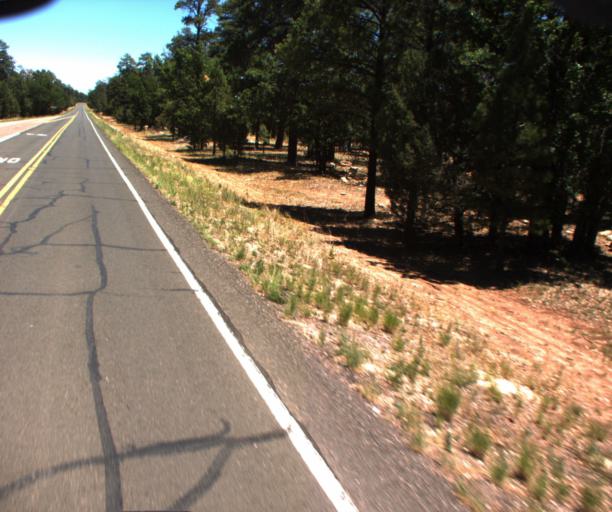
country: US
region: Arizona
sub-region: Gila County
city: Star Valley
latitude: 34.6237
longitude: -111.1560
